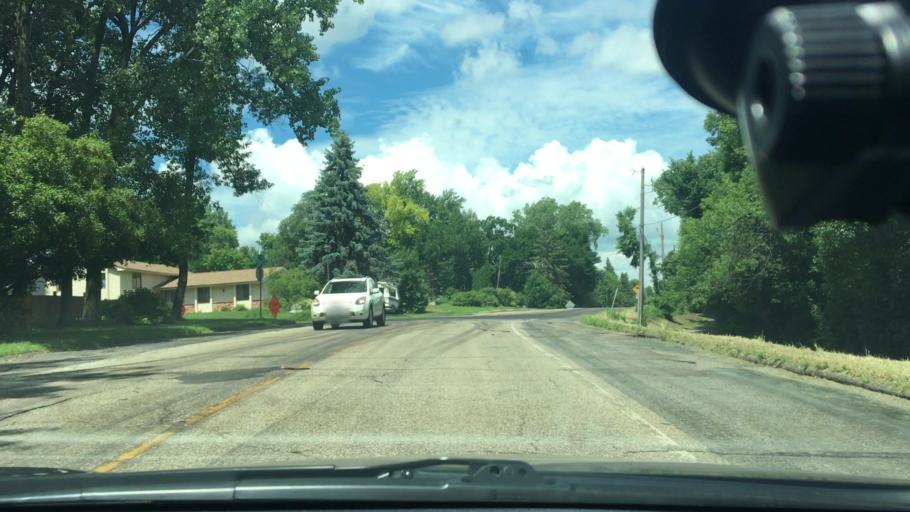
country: US
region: Minnesota
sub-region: Hennepin County
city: Plymouth
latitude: 45.0135
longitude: -93.4383
